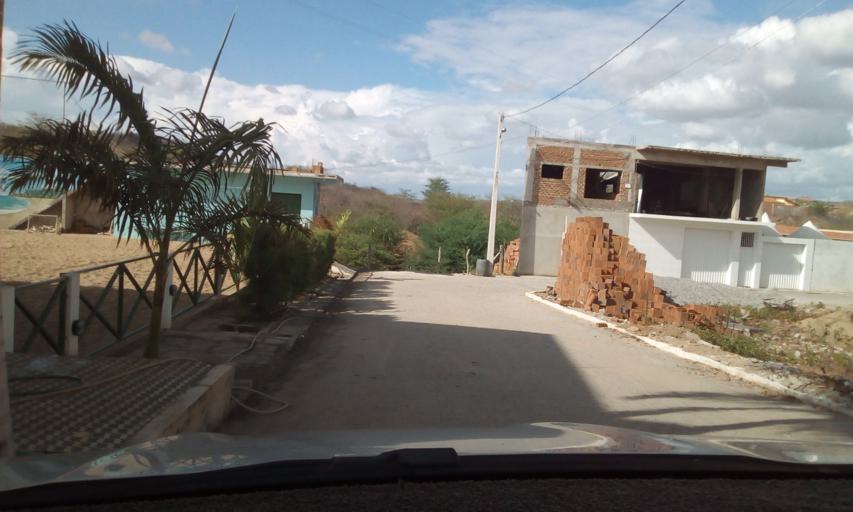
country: BR
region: Paraiba
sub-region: Picui
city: Picui
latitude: -6.5077
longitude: -36.3510
